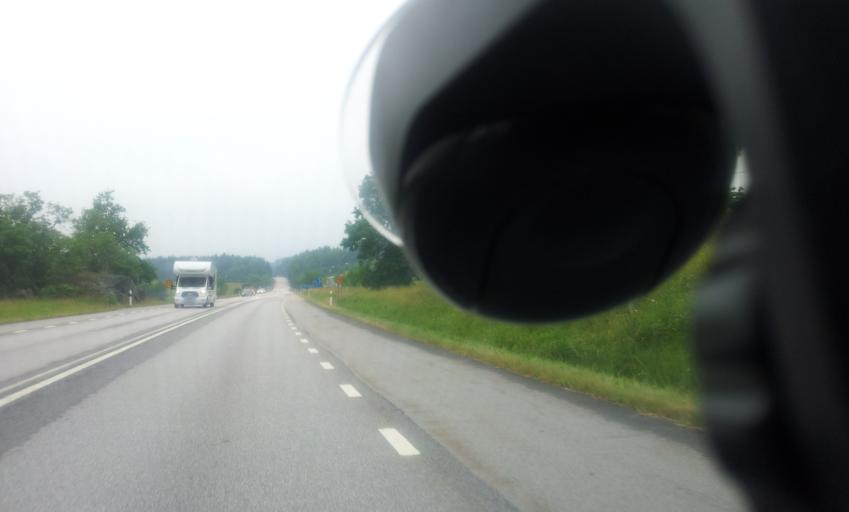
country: SE
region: Kalmar
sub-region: Vasterviks Kommun
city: Ankarsrum
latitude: 57.7131
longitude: 16.4499
